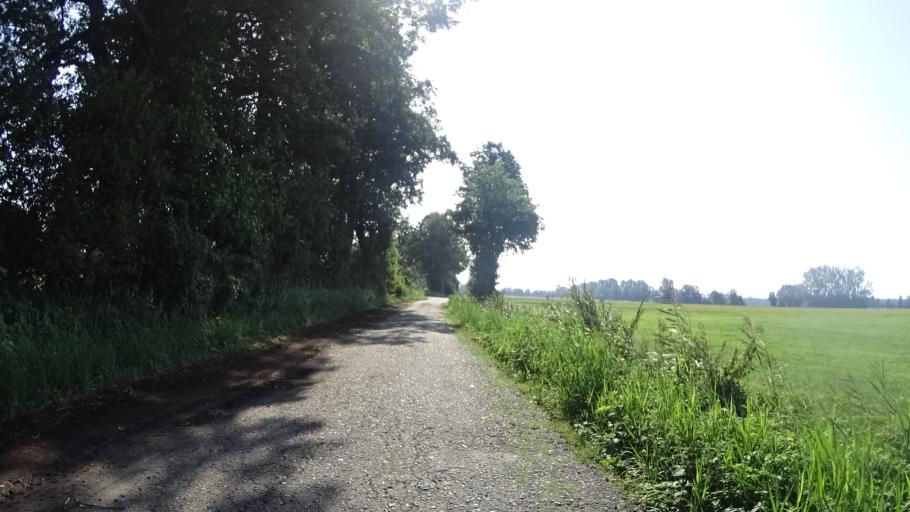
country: DE
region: Brandenburg
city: Neu Zauche
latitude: 51.9134
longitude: 14.0475
